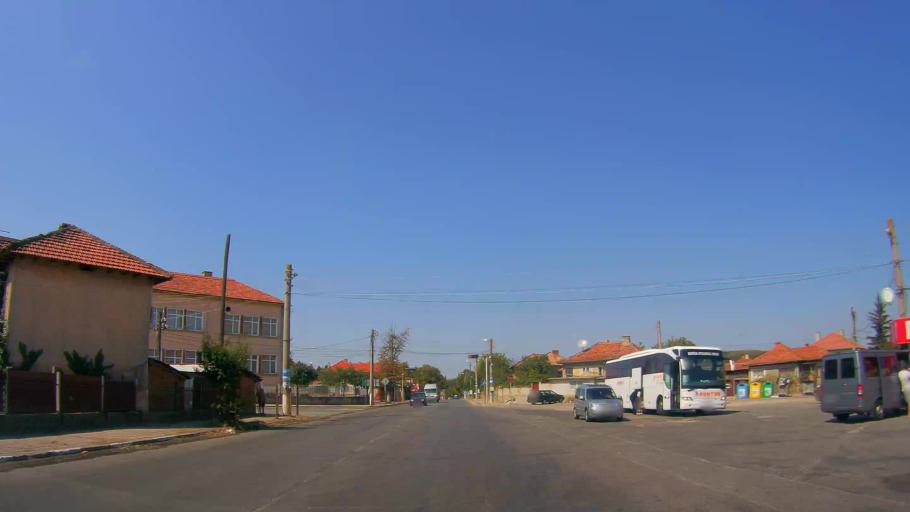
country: BG
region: Razgrad
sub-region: Obshtina Tsar Kaloyan
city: Tsar Kaloyan
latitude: 43.6057
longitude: 26.2405
